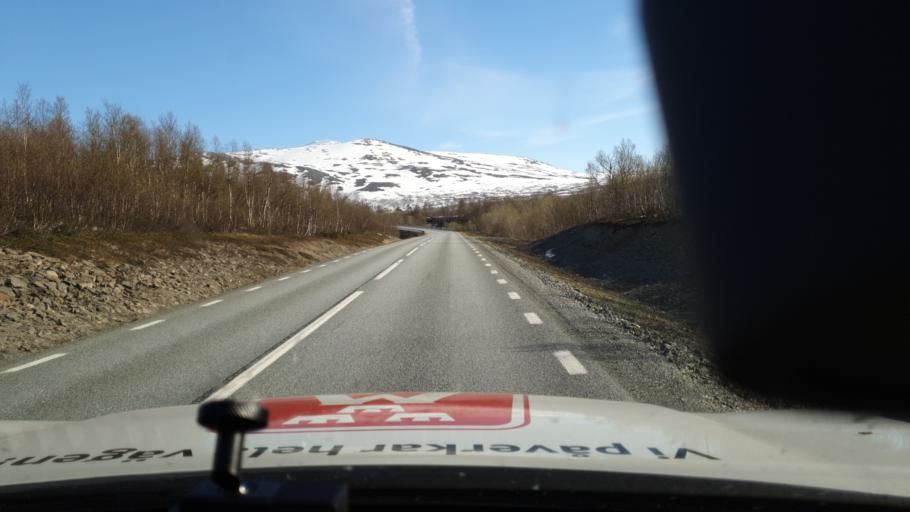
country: NO
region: Nordland
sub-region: Rana
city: Mo i Rana
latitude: 66.0610
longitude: 14.8724
